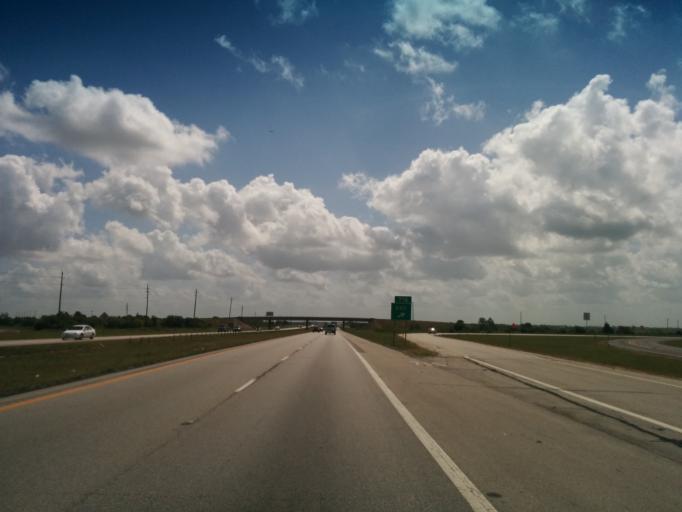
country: US
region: Texas
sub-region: Austin County
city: Sealy
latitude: 29.7580
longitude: -96.2240
